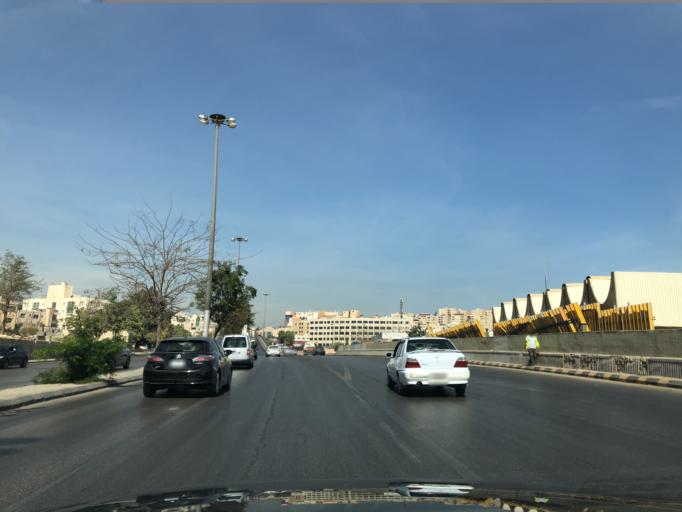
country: JO
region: Amman
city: Amman
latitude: 31.9836
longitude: 35.9006
